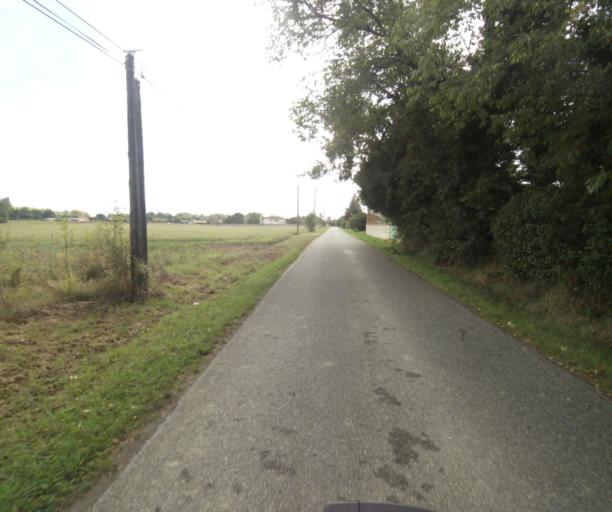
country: FR
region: Midi-Pyrenees
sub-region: Departement du Tarn-et-Garonne
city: Finhan
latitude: 43.9244
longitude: 1.2166
